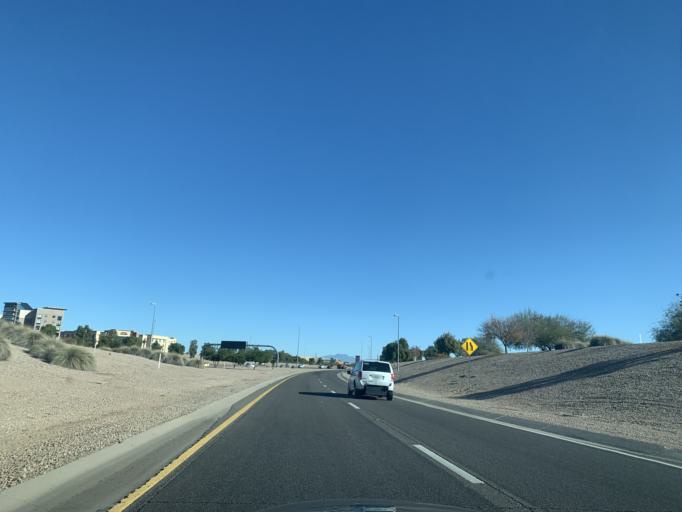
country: US
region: Arizona
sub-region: Maricopa County
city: Gilbert
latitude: 33.2885
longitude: -111.7535
